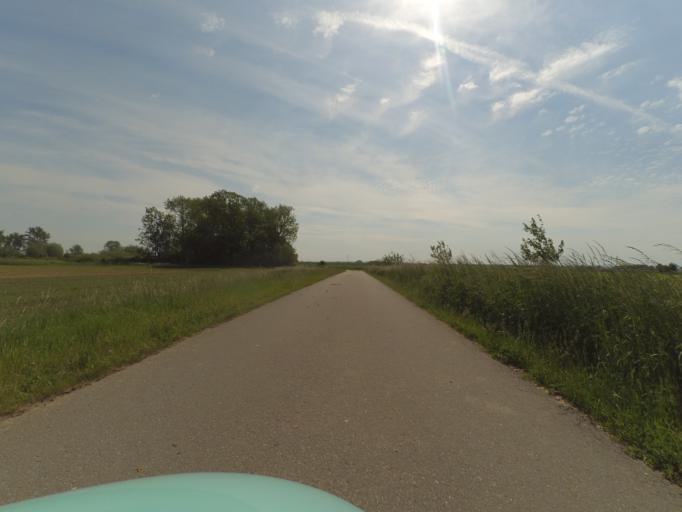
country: DE
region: Lower Saxony
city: Algermissen
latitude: 52.2824
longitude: 9.9825
